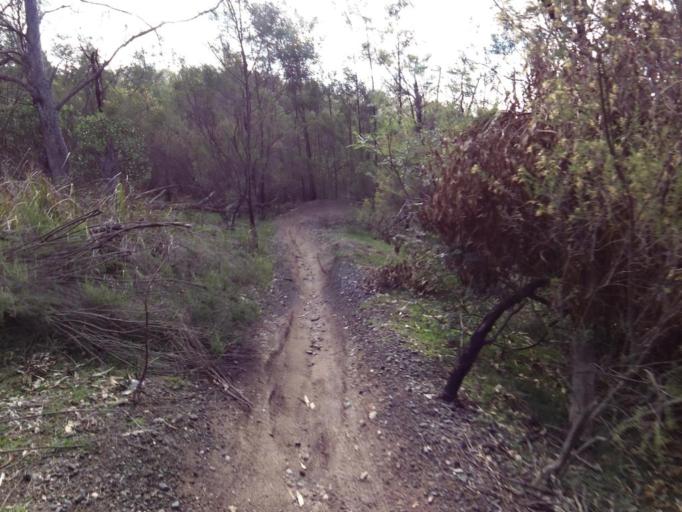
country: AU
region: Victoria
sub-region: Yarra Ranges
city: Lysterfield
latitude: -37.9449
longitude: 145.2747
